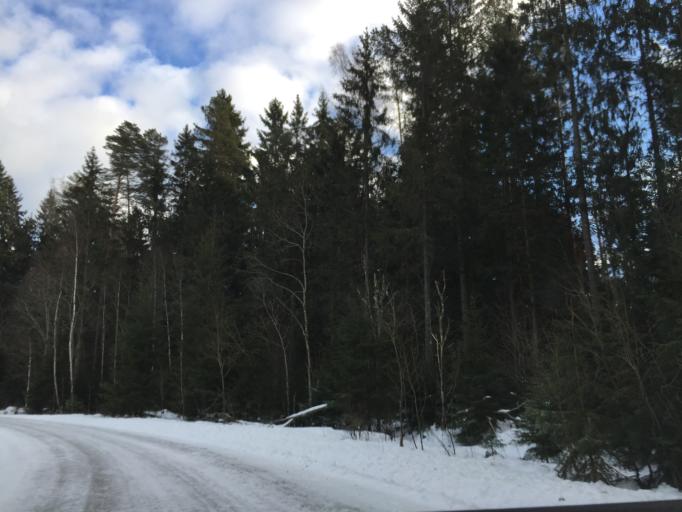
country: LV
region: Lielvarde
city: Lielvarde
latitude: 56.5620
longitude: 24.7999
